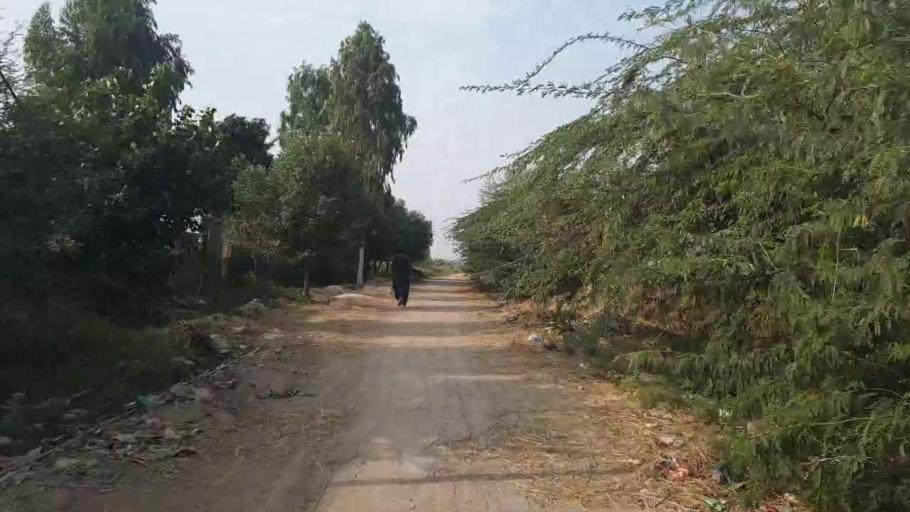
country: PK
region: Sindh
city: Tando Muhammad Khan
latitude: 25.1103
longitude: 68.5162
